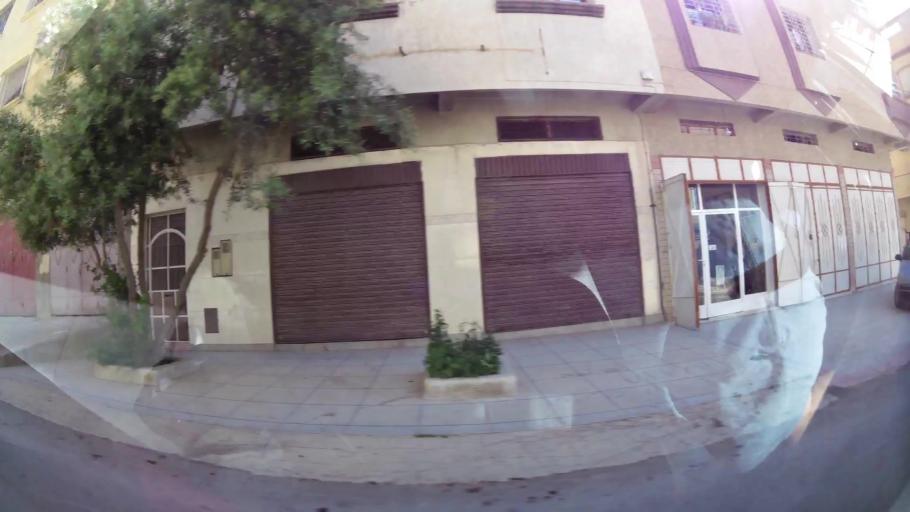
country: MA
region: Oriental
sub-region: Oujda-Angad
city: Oujda
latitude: 34.6594
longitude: -1.9196
